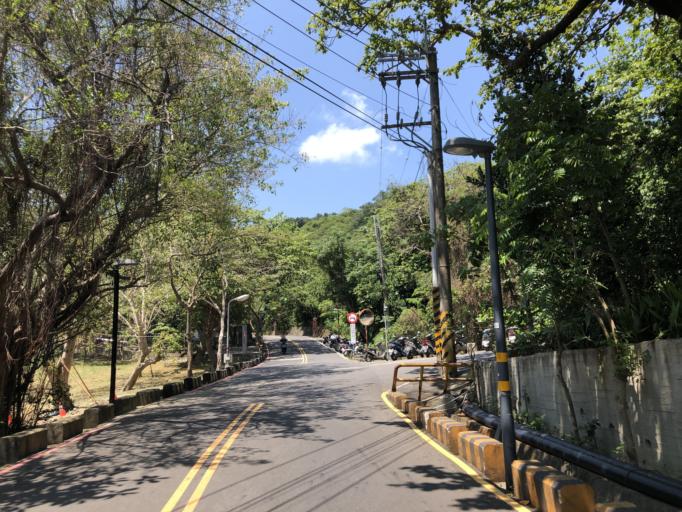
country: TW
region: Kaohsiung
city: Kaohsiung
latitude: 22.6285
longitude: 120.2693
